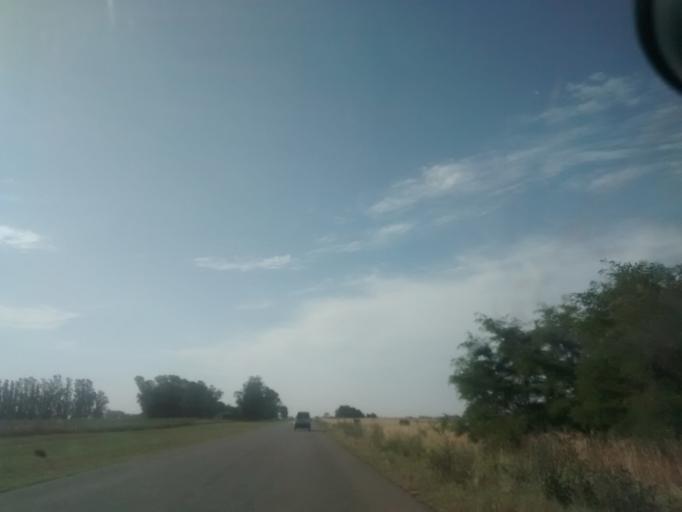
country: AR
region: Buenos Aires
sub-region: Partido de Ayacucho
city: Ayacucho
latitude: -37.1615
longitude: -58.5385
